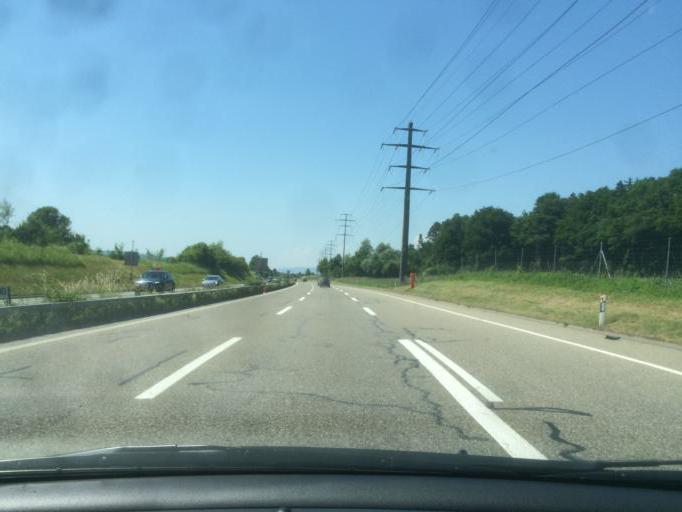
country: CH
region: Zurich
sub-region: Bezirk Uster
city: Uster / Gschwader
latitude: 47.3711
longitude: 8.7076
